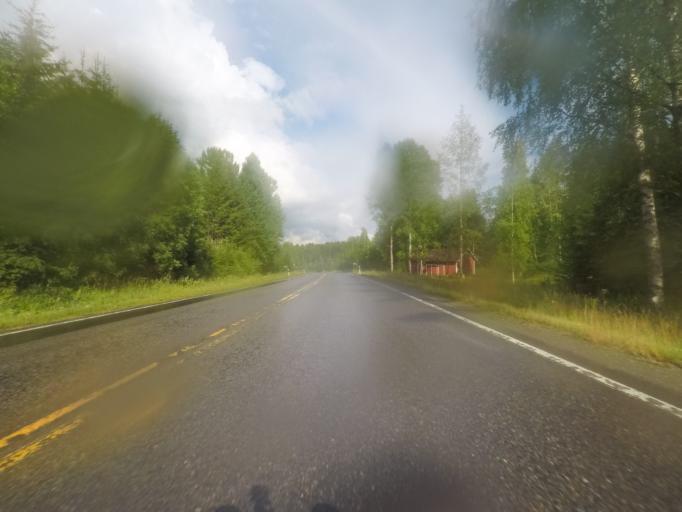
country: FI
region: Southern Savonia
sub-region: Pieksaemaeki
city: Juva
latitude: 61.8984
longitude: 27.9507
